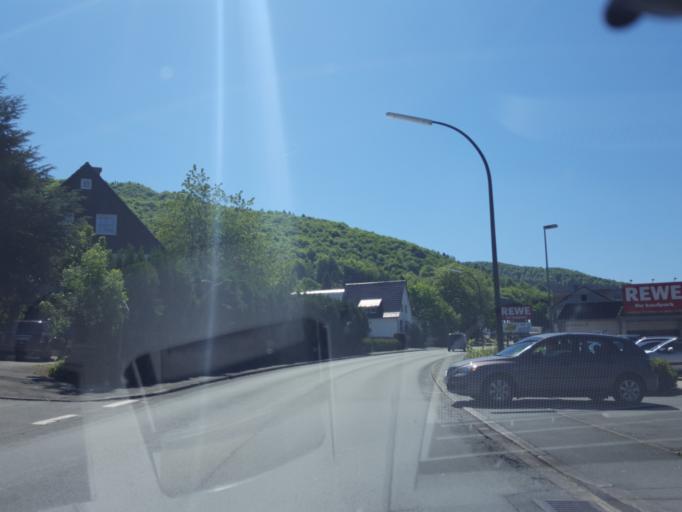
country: DE
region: North Rhine-Westphalia
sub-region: Regierungsbezirk Arnsberg
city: Winterberg
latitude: 51.2500
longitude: 8.4809
